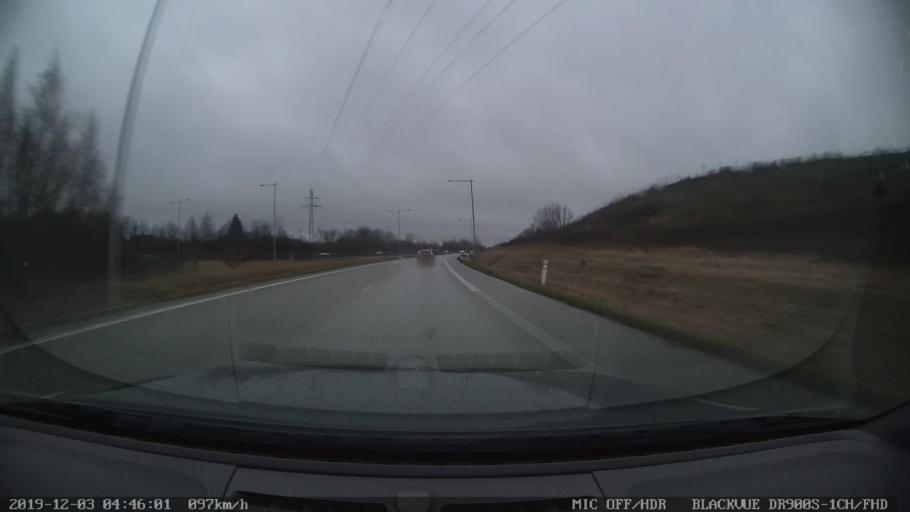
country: SE
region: Skane
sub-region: Burlovs Kommun
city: Arloev
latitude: 55.6397
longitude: 13.1005
